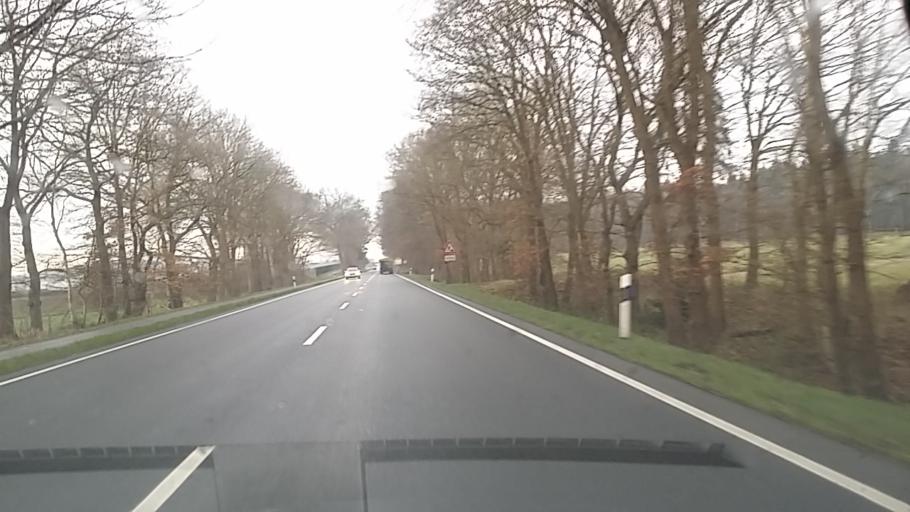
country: DE
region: Lower Saxony
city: Loningen
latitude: 52.7552
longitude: 7.7784
